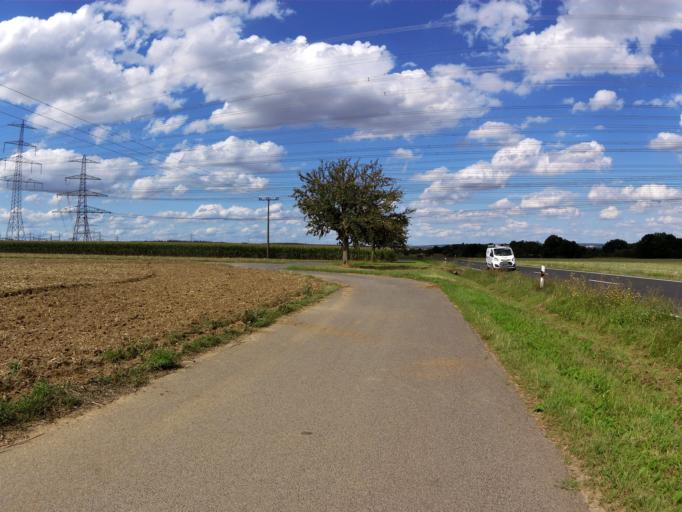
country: DE
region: Bavaria
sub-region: Regierungsbezirk Unterfranken
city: Bergrheinfeld
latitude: 49.9844
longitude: 10.1695
